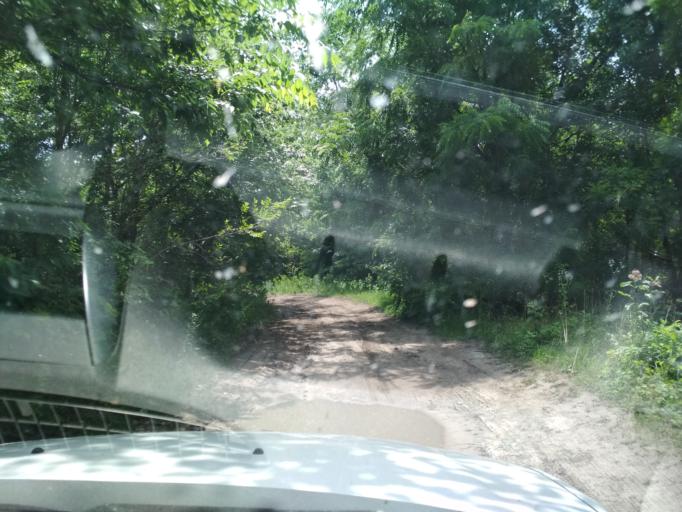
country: HU
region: Pest
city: Tapioszentmarton
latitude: 47.3615
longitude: 19.7431
